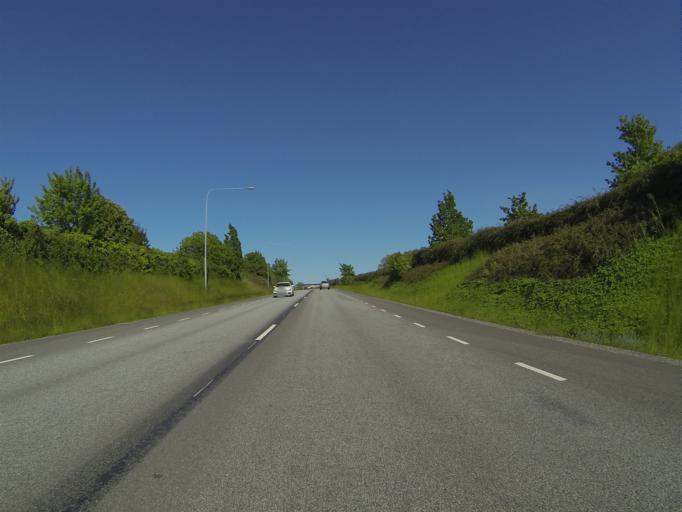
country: SE
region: Skane
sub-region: Burlovs Kommun
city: Arloev
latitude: 55.5944
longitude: 13.0790
